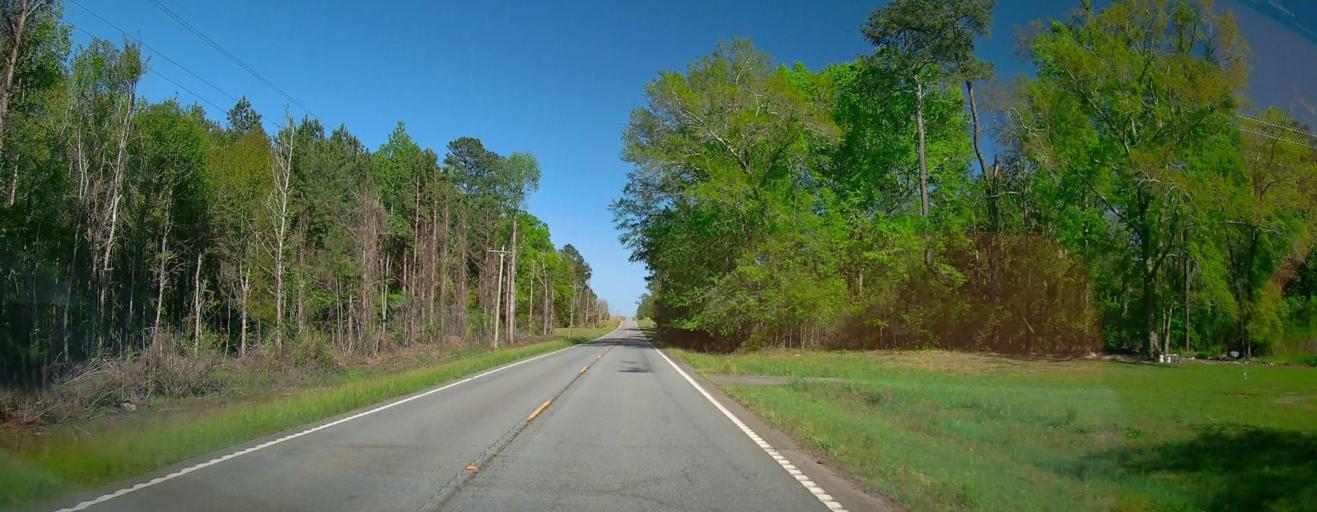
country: US
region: Georgia
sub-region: Dooly County
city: Unadilla
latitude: 32.2600
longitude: -83.6843
